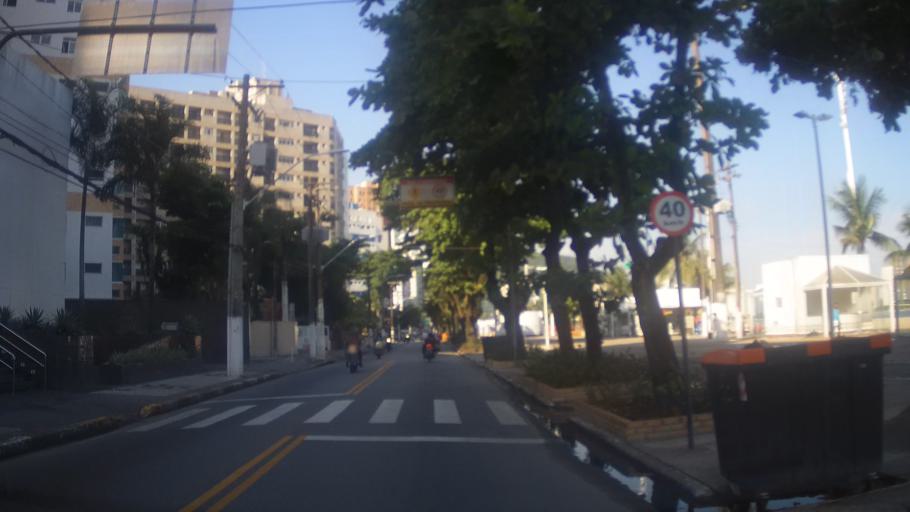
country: BR
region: Sao Paulo
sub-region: Sao Vicente
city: Sao Vicente
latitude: -23.9706
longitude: -46.3849
